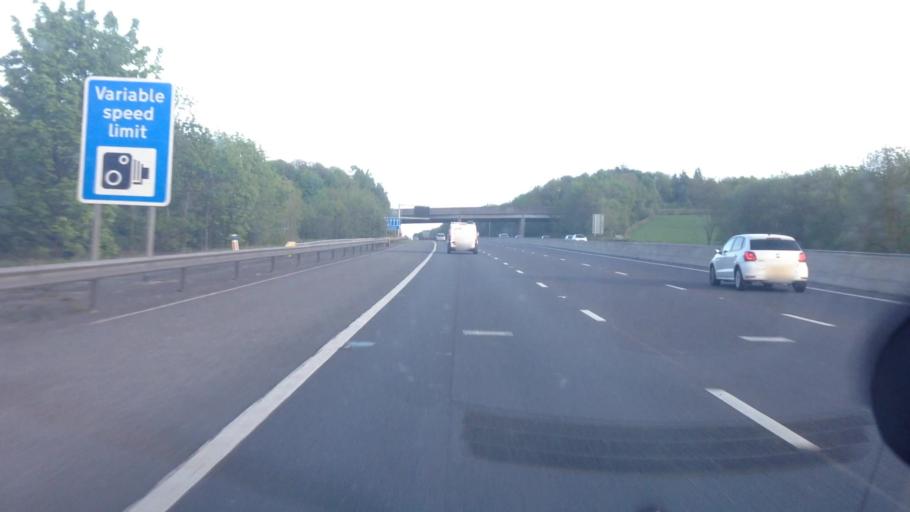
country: GB
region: England
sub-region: Sheffield
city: Chapletown
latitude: 53.4814
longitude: -1.4647
